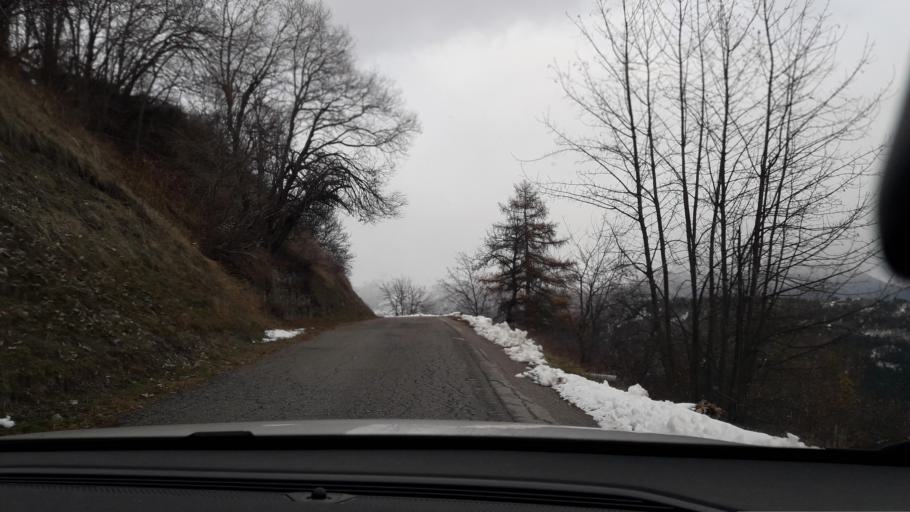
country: FR
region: Rhone-Alpes
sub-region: Departement de la Savoie
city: Valloire
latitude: 45.2021
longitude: 6.4161
